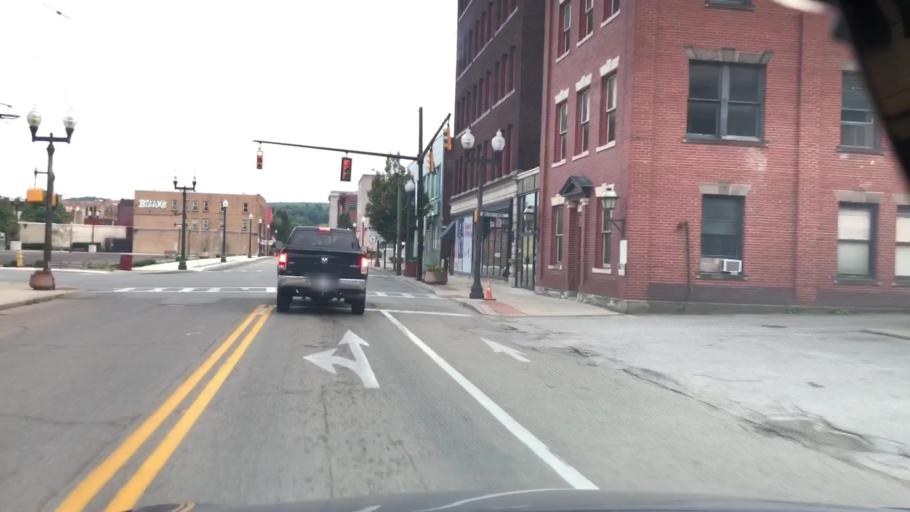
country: US
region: Pennsylvania
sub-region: Venango County
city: Oil City
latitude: 41.4372
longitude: -79.7093
